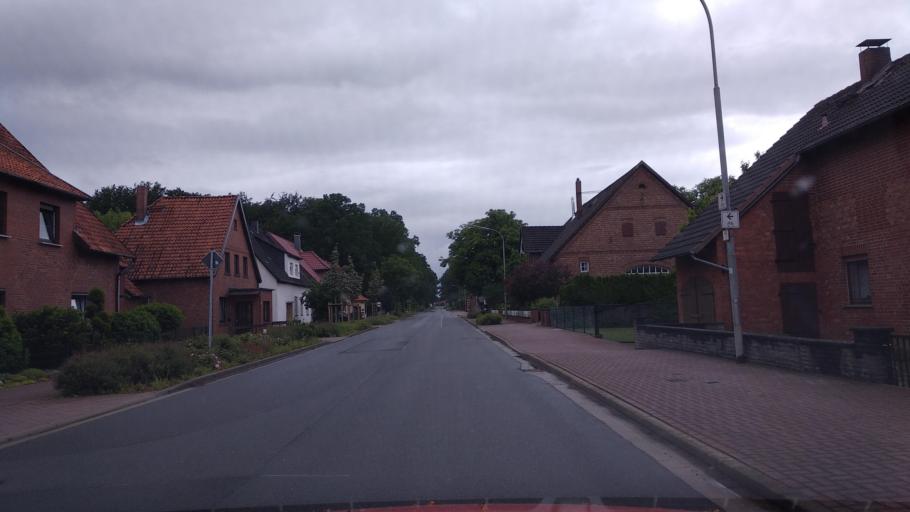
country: DE
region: Lower Saxony
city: Auhagen
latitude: 52.3920
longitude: 9.2835
